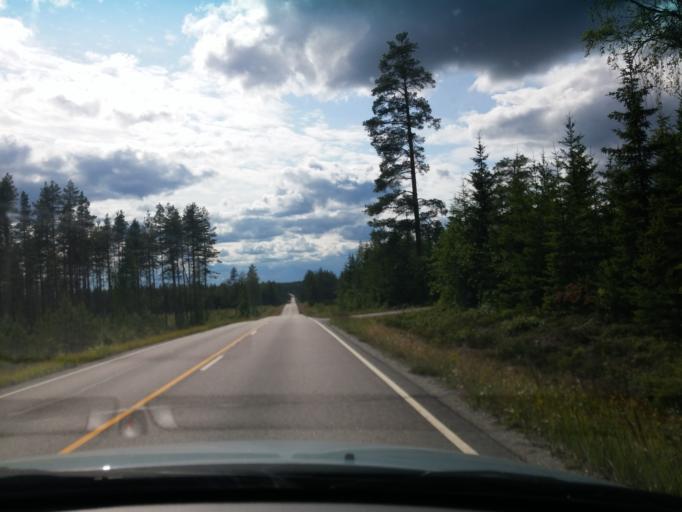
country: FI
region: Central Finland
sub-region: Saarijaervi-Viitasaari
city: Pylkoenmaeki
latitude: 62.5992
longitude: 24.6316
